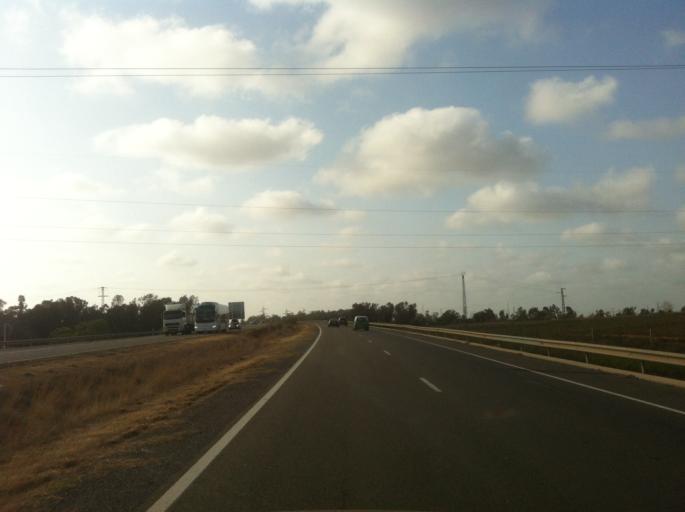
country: MA
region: Gharb-Chrarda-Beni Hssen
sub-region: Kenitra Province
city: Kenitra
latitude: 34.2230
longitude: -6.5366
